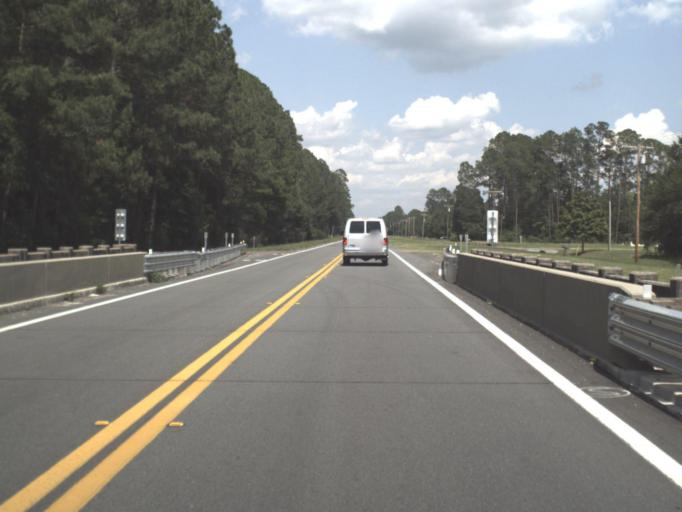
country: US
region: Florida
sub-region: Bradford County
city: Starke
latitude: 29.9386
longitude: -82.0784
